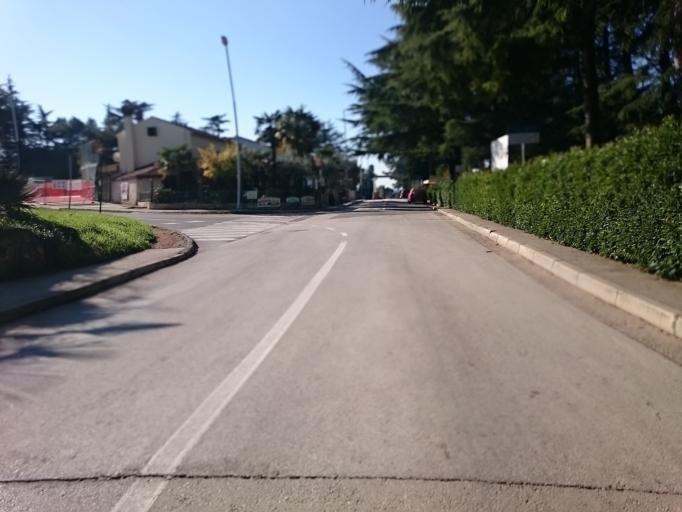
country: HR
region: Istarska
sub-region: Grad Porec
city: Porec
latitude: 45.2413
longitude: 13.6006
